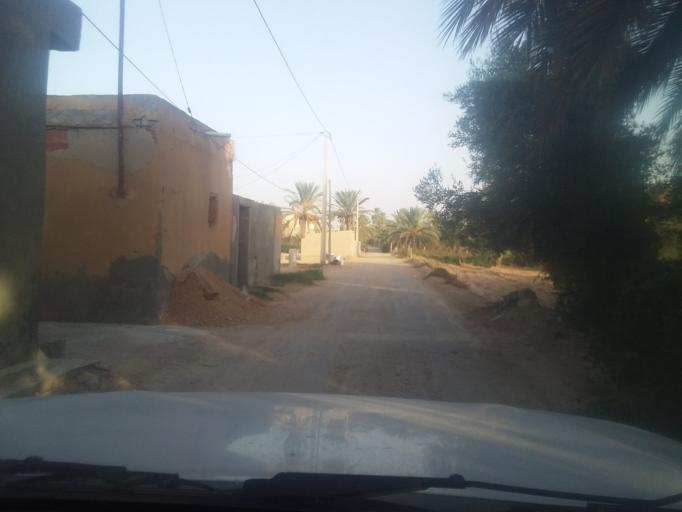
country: TN
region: Qabis
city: Gabes
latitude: 33.6298
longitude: 10.2876
